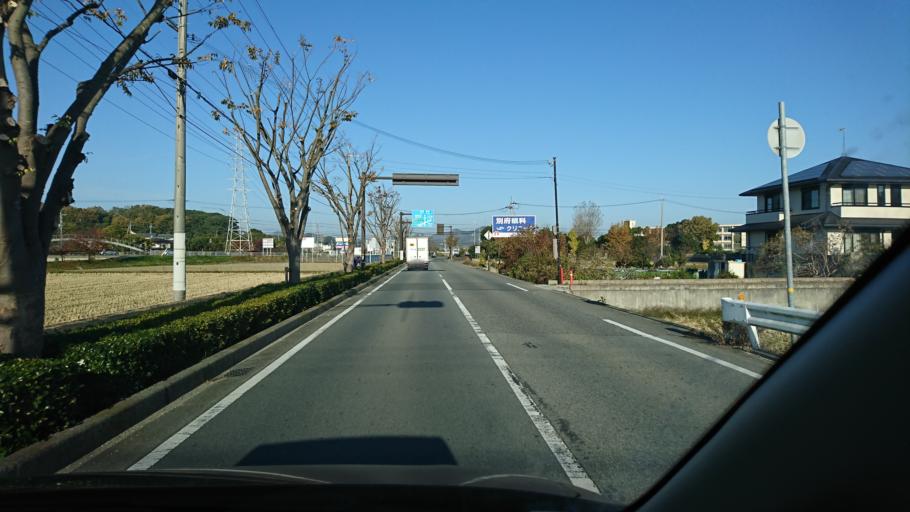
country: JP
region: Hyogo
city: Kakogawacho-honmachi
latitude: 34.7736
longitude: 134.8784
